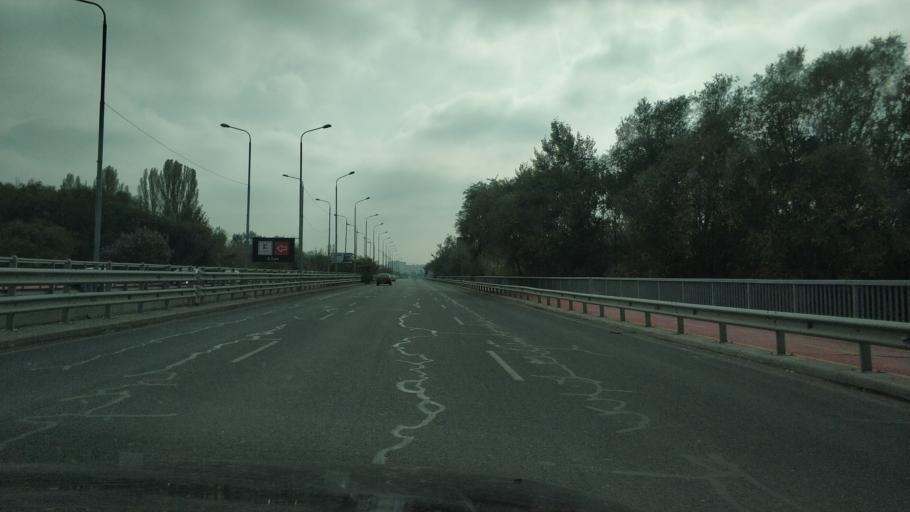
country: BG
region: Plovdiv
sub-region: Obshtina Plovdiv
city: Plovdiv
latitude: 42.1573
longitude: 24.7652
